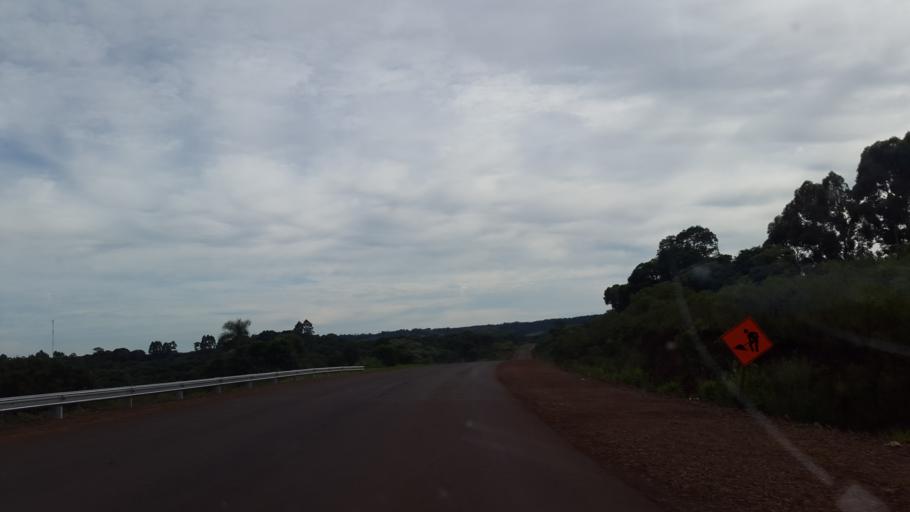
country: AR
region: Misiones
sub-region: Departamento de San Pedro
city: San Pedro
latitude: -26.4843
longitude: -53.8882
